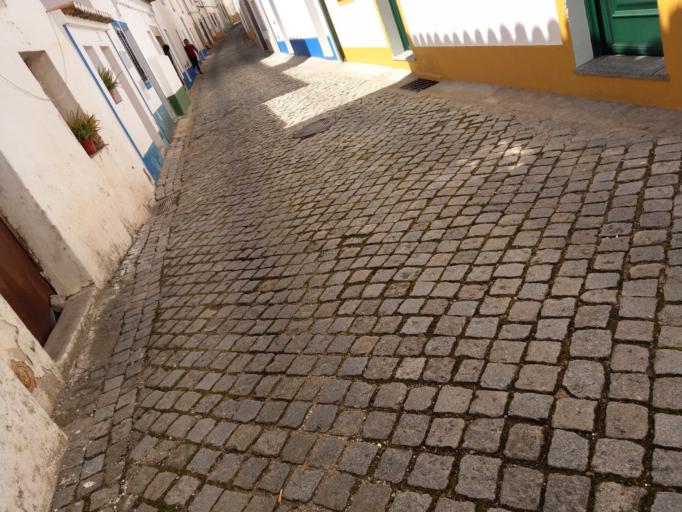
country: PT
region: Portalegre
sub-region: Arronches
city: Arronches
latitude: 39.1232
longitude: -7.2834
